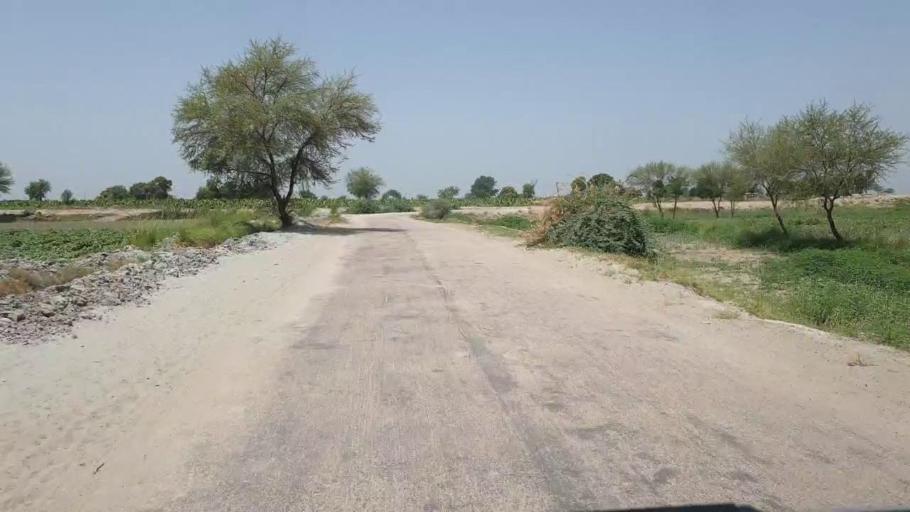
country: PK
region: Sindh
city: Nawabshah
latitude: 26.3439
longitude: 68.3856
